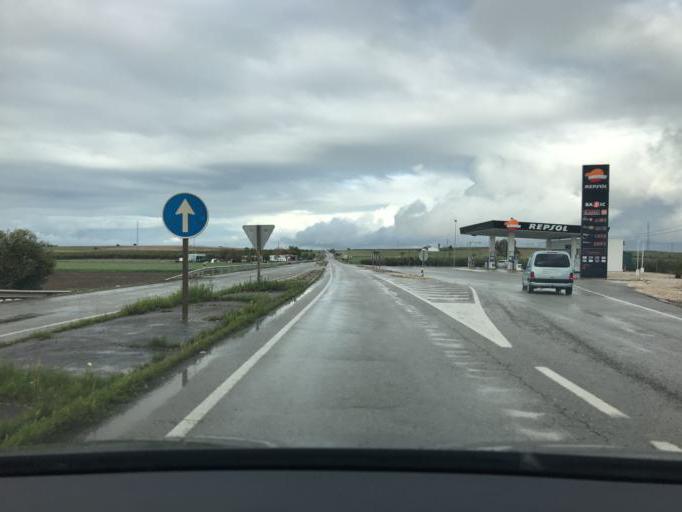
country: ES
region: Andalusia
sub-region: Provincia de Sevilla
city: La Luisiana
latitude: 37.4892
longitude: -5.1660
